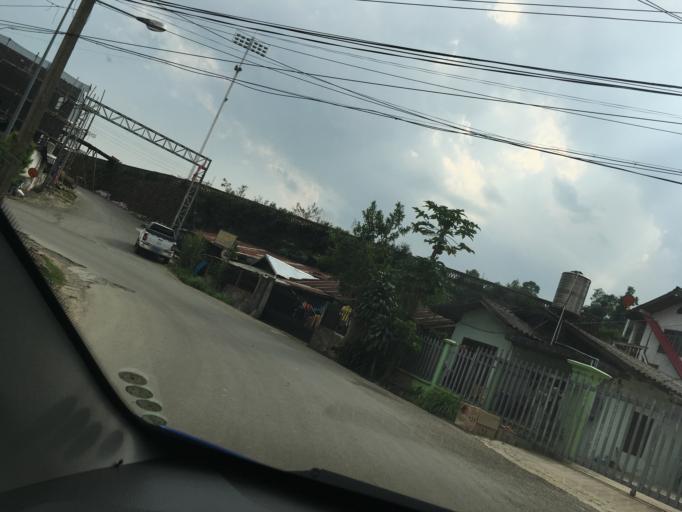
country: LA
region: Phongsali
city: Phongsali
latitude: 21.6835
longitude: 102.1002
